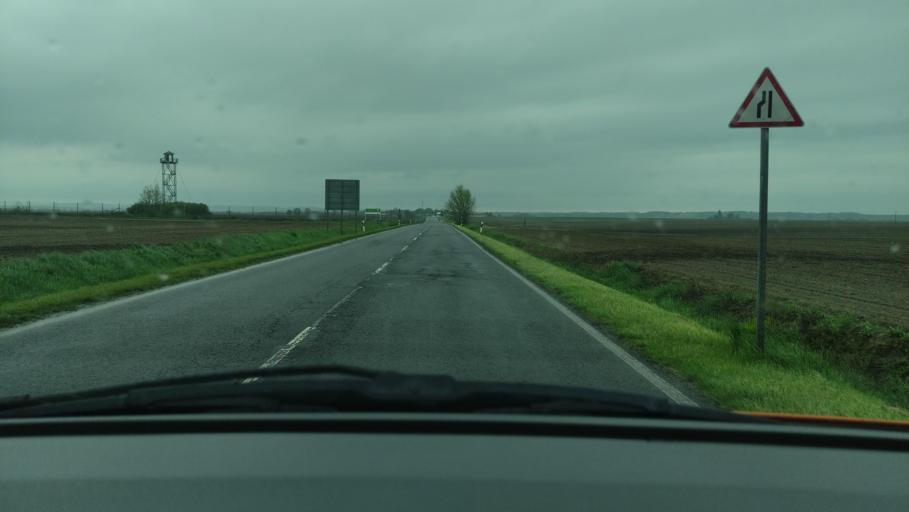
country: HU
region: Baranya
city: Mohacs
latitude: 45.9182
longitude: 18.6594
